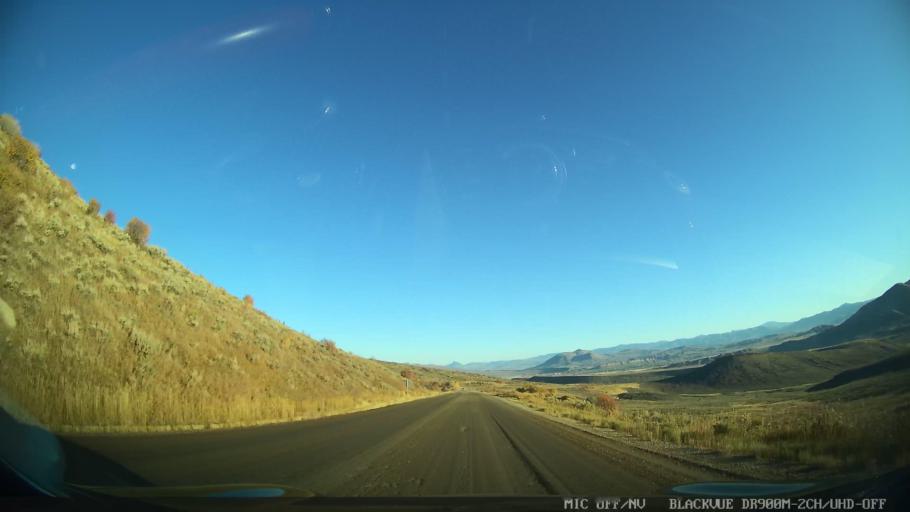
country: US
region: Colorado
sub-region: Grand County
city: Kremmling
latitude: 39.9996
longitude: -106.4051
